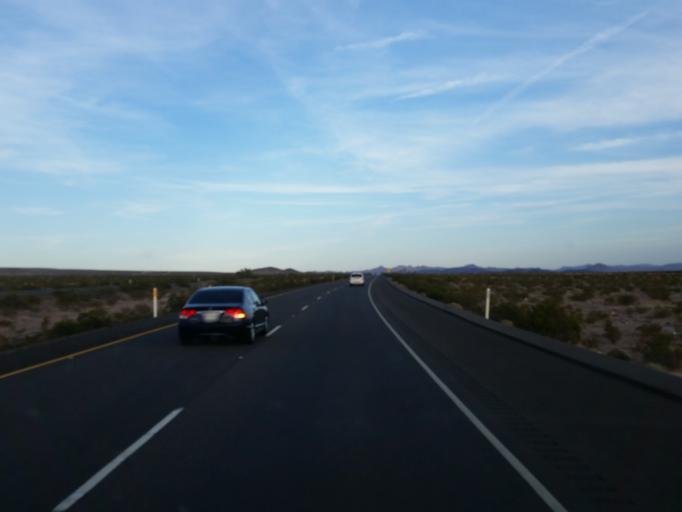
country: US
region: California
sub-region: San Bernardino County
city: Fort Irwin
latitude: 34.7698
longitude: -116.3622
